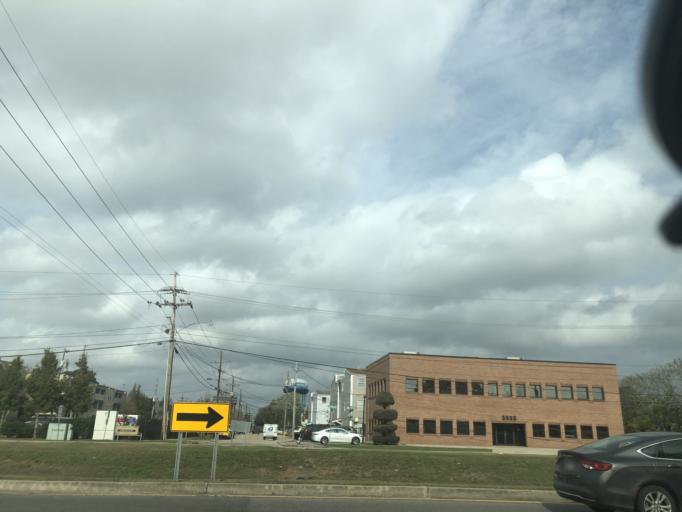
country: US
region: Louisiana
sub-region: Jefferson Parish
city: Metairie
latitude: 29.9921
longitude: -90.1587
